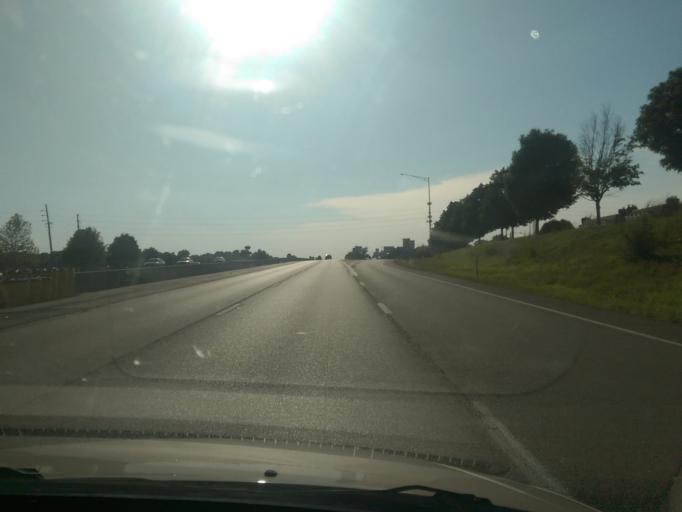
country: US
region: Missouri
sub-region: Jackson County
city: Blue Springs
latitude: 39.0298
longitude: -94.2674
